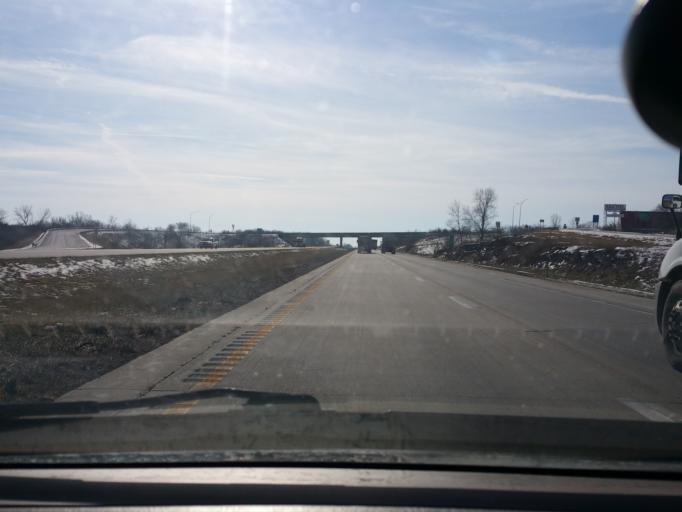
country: US
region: Missouri
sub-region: Clinton County
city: Cameron
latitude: 39.6710
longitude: -94.2349
